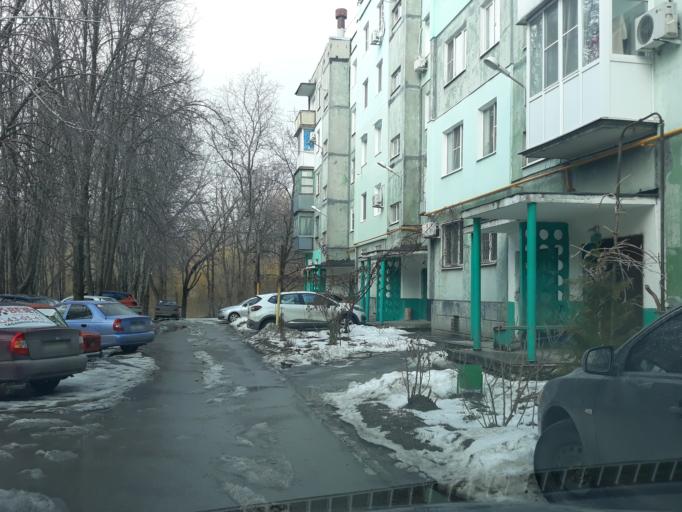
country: RU
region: Rostov
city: Taganrog
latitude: 47.2531
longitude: 38.9141
